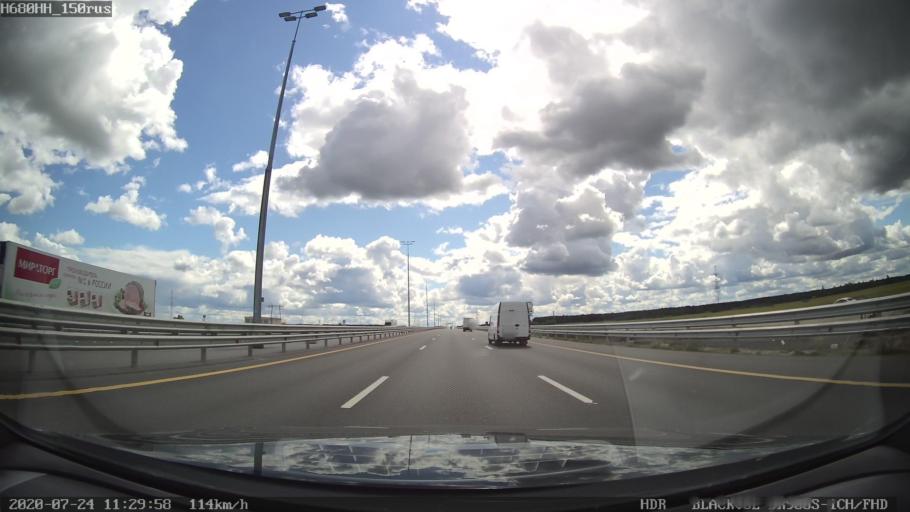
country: RU
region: Leningrad
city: Krasnyy Bor
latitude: 59.6750
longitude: 30.6026
